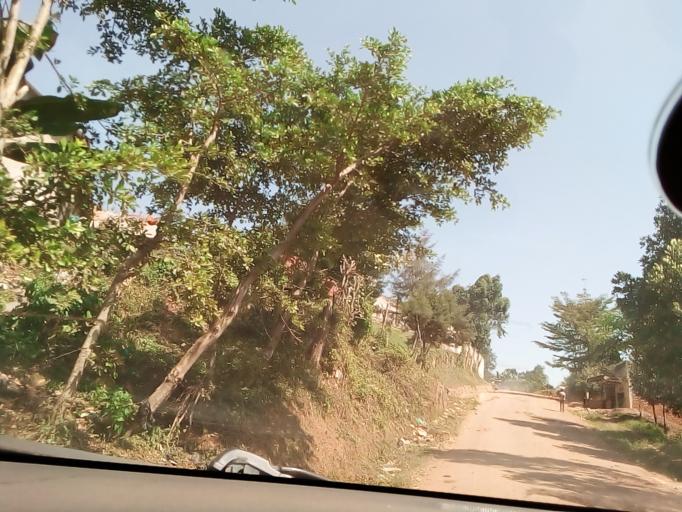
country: UG
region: Central Region
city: Masaka
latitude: -0.3483
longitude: 31.7441
